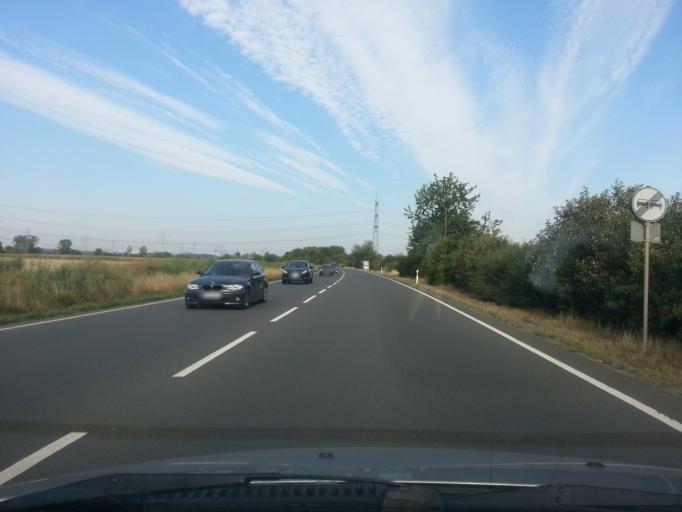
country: DE
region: Hesse
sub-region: Regierungsbezirk Darmstadt
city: Burstadt
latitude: 49.6377
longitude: 8.4399
